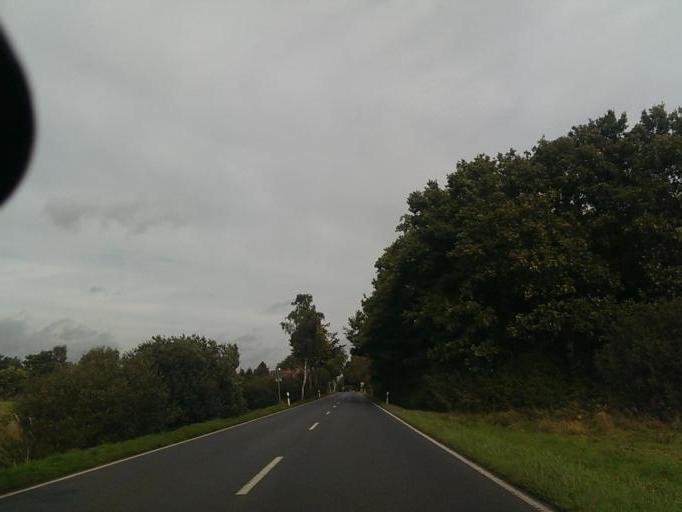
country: DE
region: Lower Saxony
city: Garbsen-Mitte
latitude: 52.4931
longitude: 9.6331
